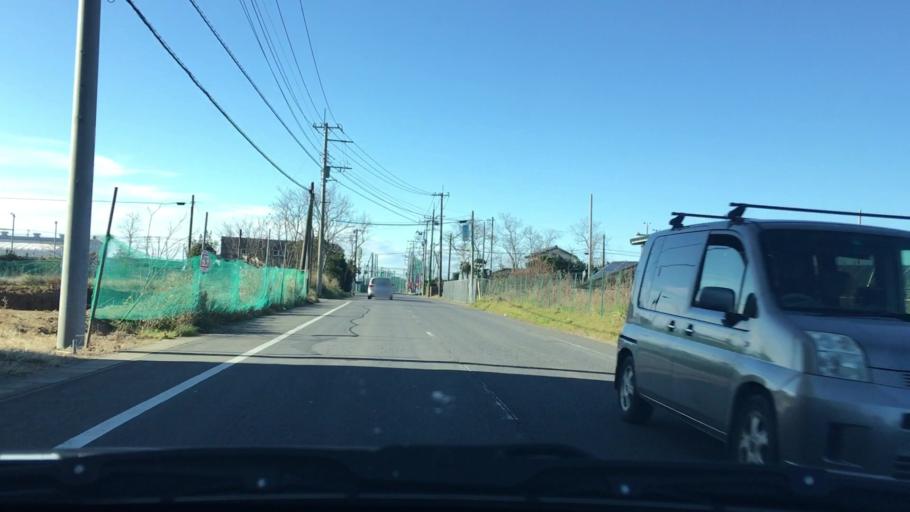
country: JP
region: Chiba
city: Omigawa
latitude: 35.8657
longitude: 140.7133
